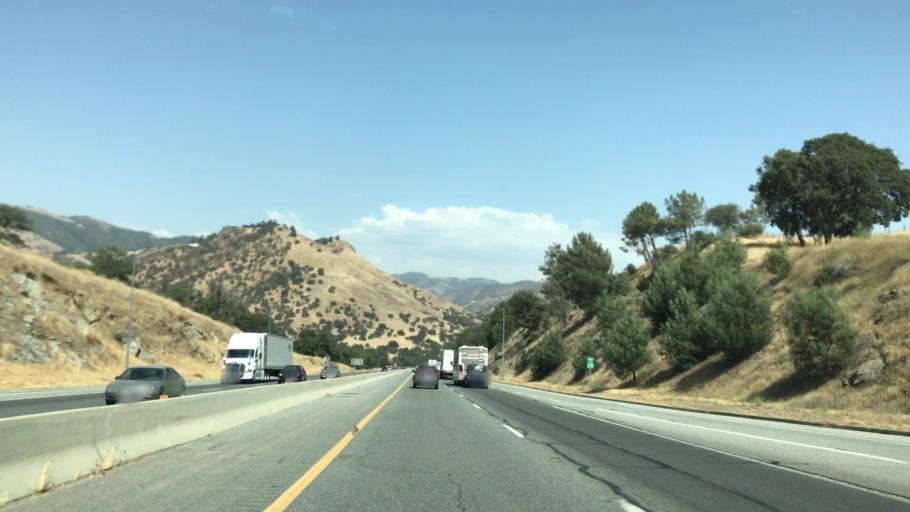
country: US
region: California
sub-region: Kern County
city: Bear Valley Springs
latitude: 35.2404
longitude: -118.5856
